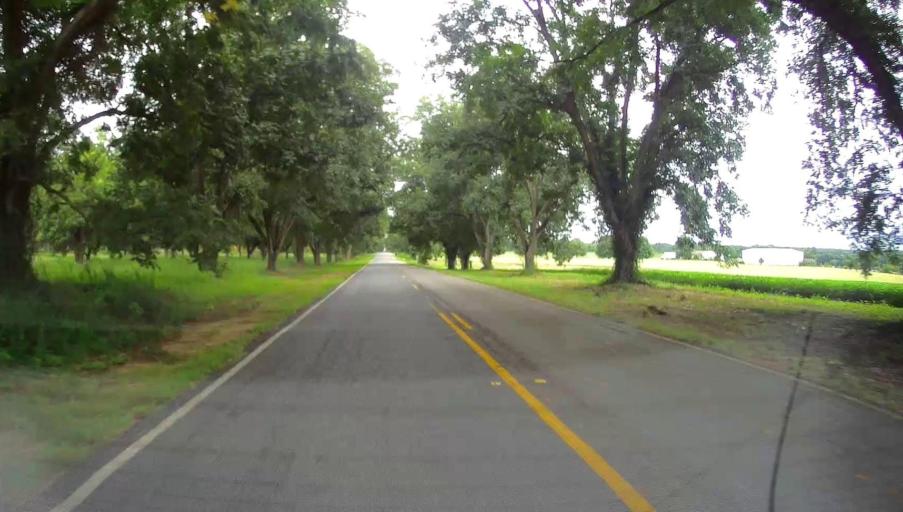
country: US
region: Georgia
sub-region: Dooly County
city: Unadilla
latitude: 32.2915
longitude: -83.8786
